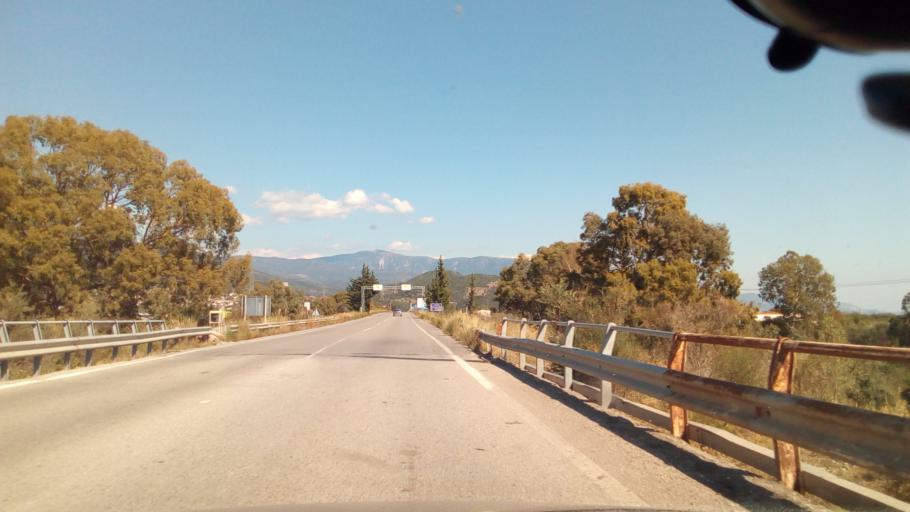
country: GR
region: West Greece
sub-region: Nomos Aitolias kai Akarnanias
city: Nafpaktos
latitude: 38.4074
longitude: 21.8778
